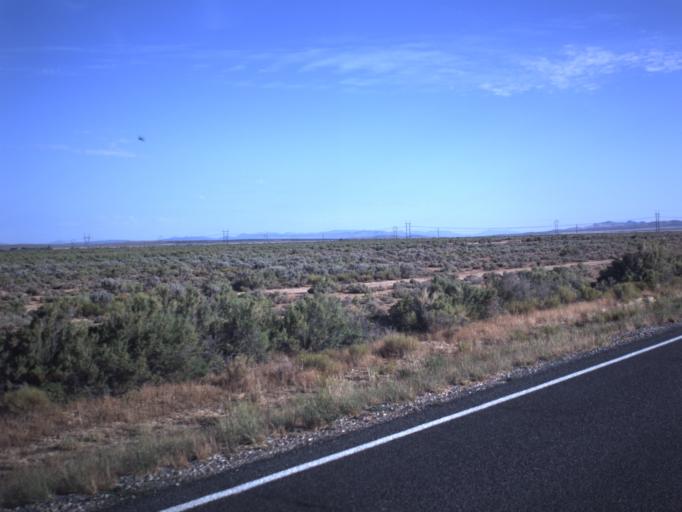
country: US
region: Utah
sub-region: Iron County
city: Enoch
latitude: 37.7926
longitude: -113.0506
